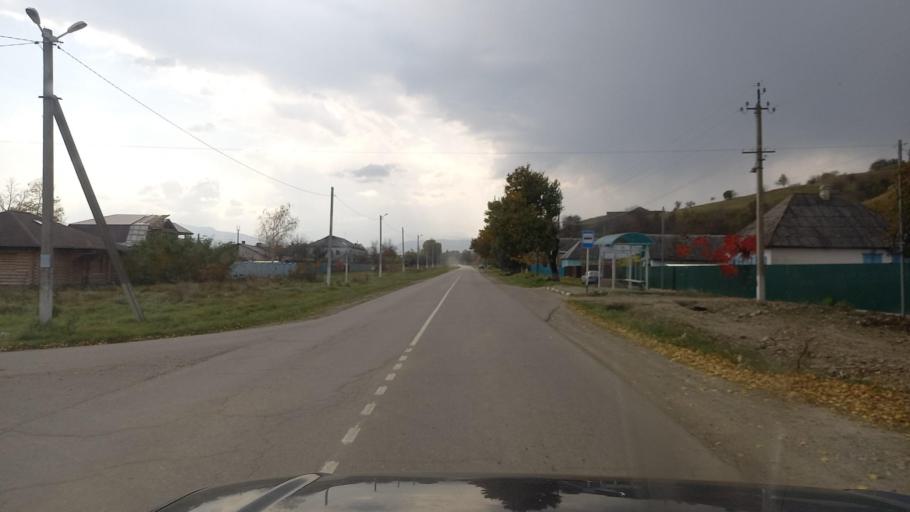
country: RU
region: Krasnodarskiy
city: Psebay
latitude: 44.1387
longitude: 40.8194
